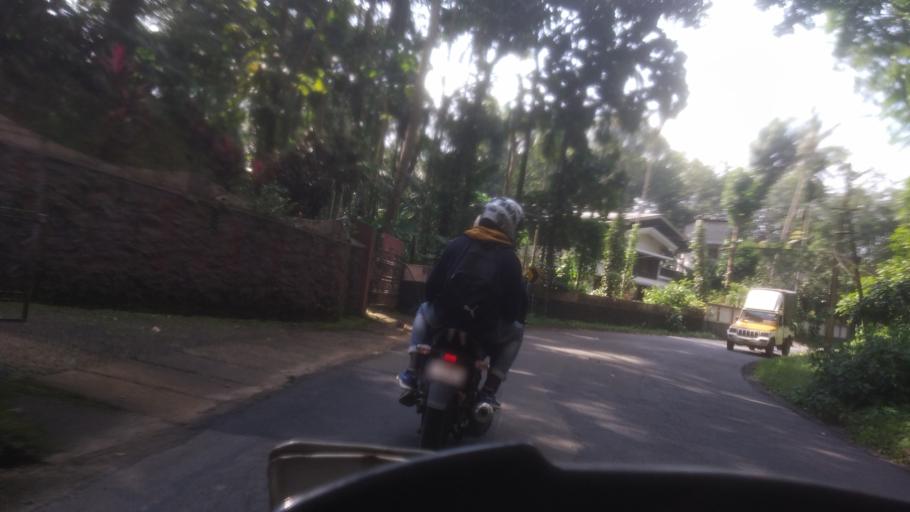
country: IN
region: Kerala
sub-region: Ernakulam
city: Kotamangalam
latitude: 10.0070
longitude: 76.7150
